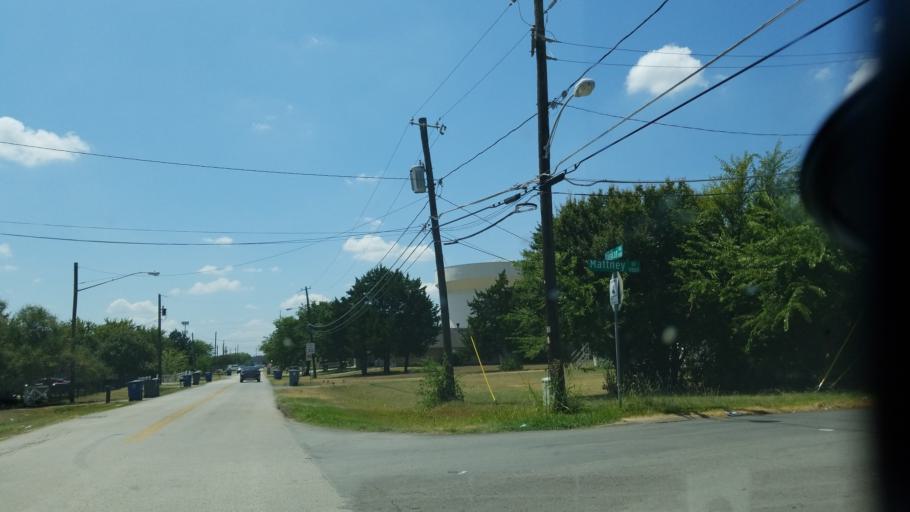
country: US
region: Texas
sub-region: Dallas County
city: Duncanville
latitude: 32.6649
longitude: -96.8841
